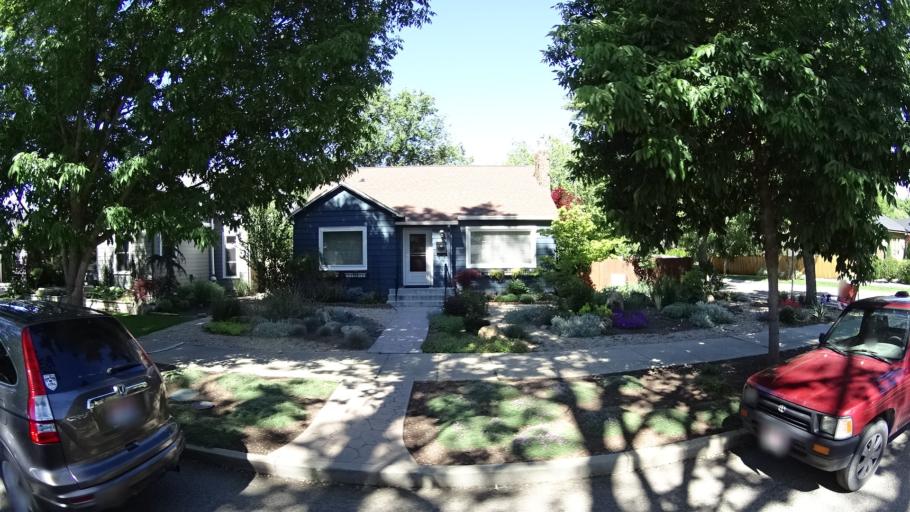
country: US
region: Idaho
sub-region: Ada County
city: Boise
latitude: 43.6363
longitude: -116.2134
